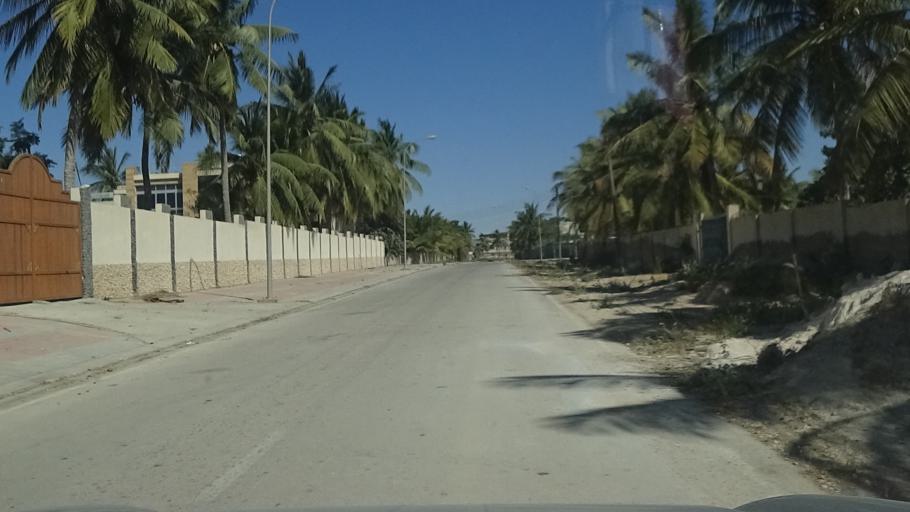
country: OM
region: Zufar
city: Salalah
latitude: 17.0278
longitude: 54.1625
